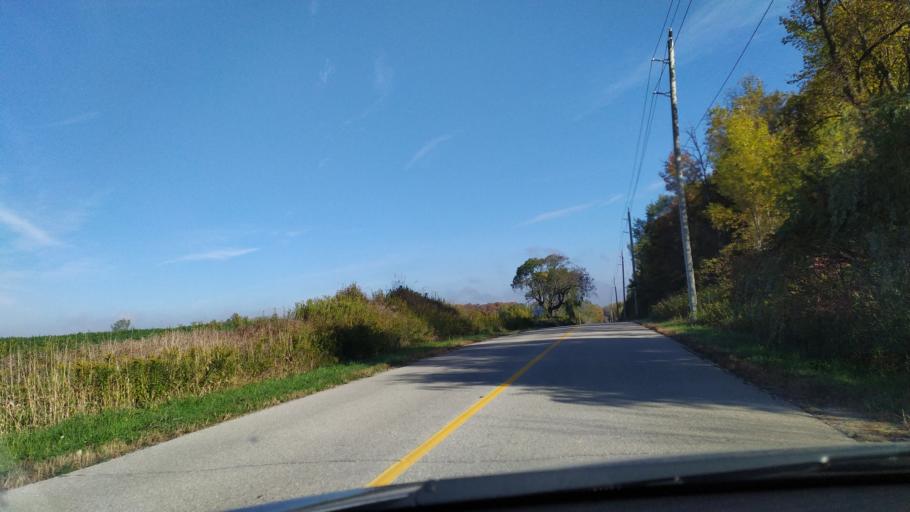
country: CA
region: Ontario
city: Waterloo
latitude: 43.4880
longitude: -80.6578
